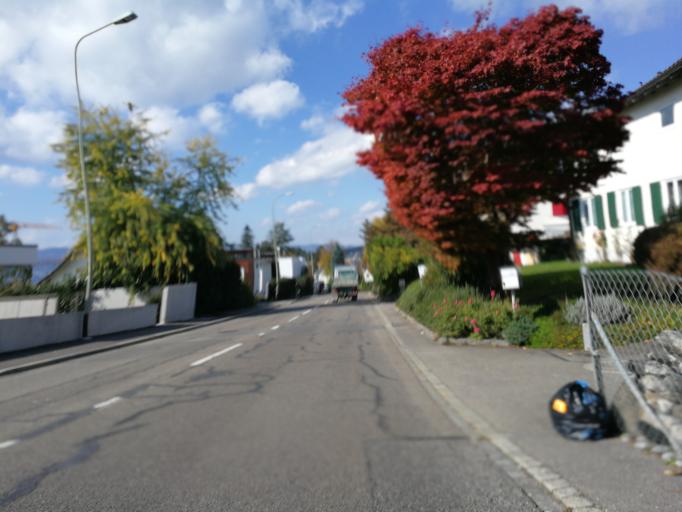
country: CH
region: Zurich
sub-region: Bezirk Meilen
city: Maennedorf / Dorfkern
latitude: 47.2608
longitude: 8.6899
